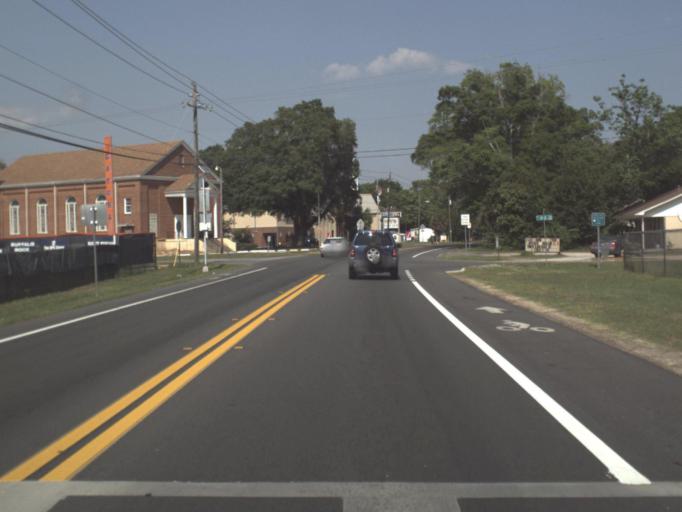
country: US
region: Florida
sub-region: Escambia County
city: Myrtle Grove
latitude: 30.4242
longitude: -87.2967
